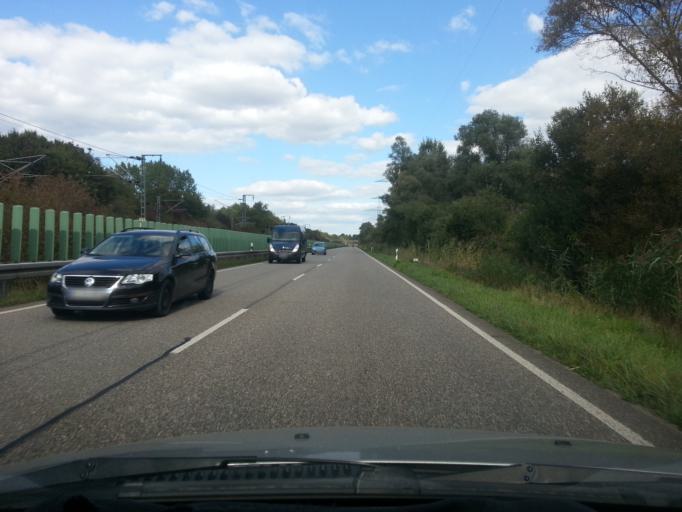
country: DE
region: Baden-Wuerttemberg
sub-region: Karlsruhe Region
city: Waghausel
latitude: 49.2639
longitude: 8.5089
